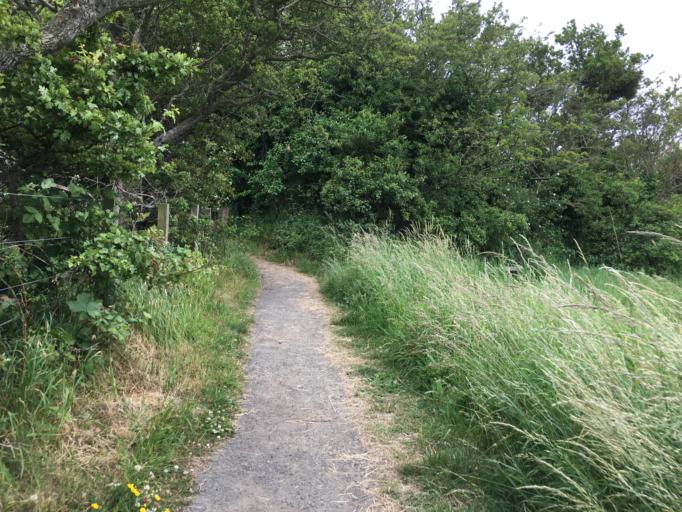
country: GB
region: England
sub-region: Northumberland
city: Alnmouth
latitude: 55.3887
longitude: -1.6176
